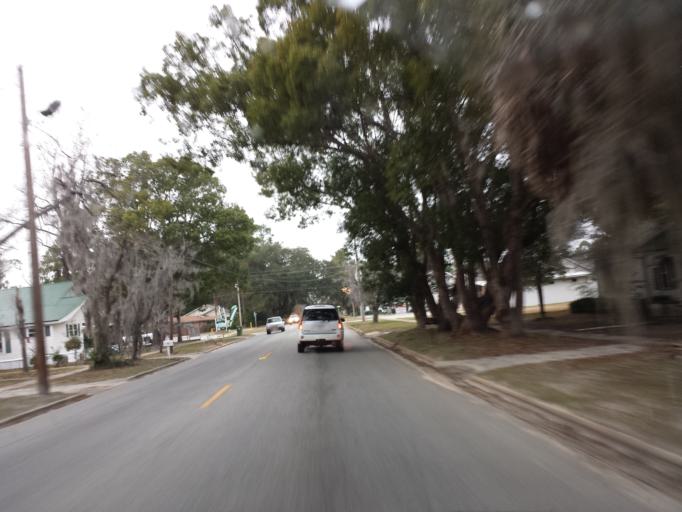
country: US
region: Georgia
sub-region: Cook County
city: Adel
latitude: 31.1298
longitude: -83.4208
